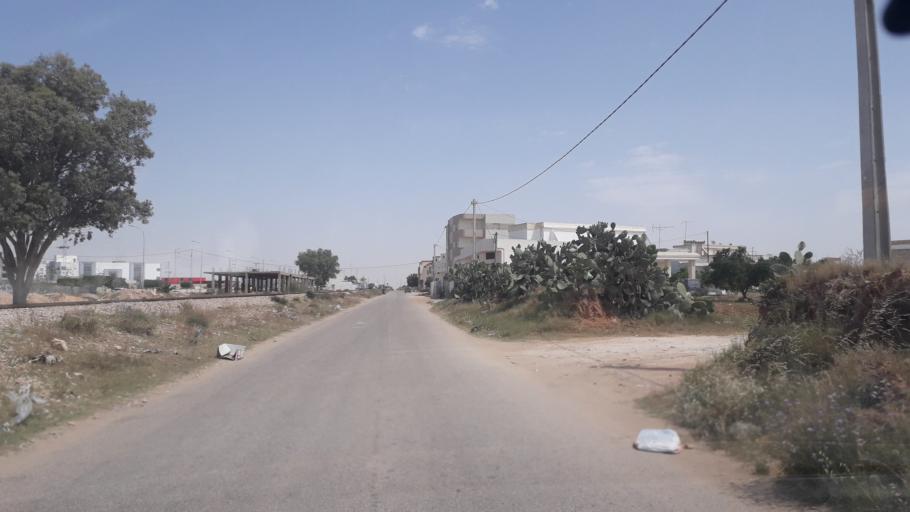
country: TN
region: Safaqis
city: Al Qarmadah
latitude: 34.8321
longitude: 10.7651
